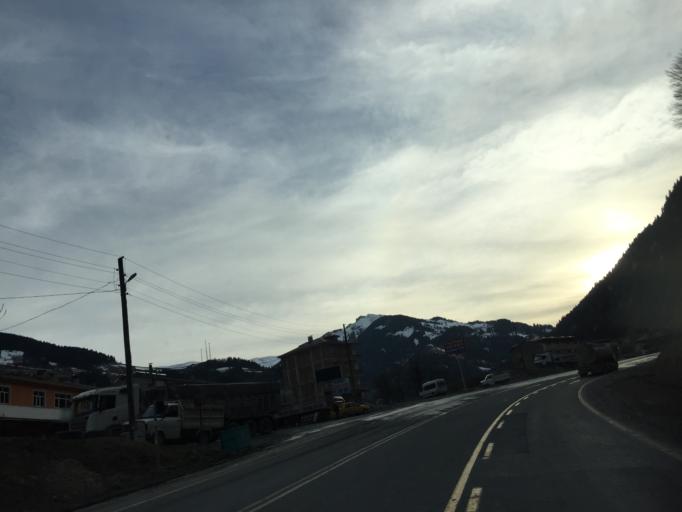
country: TR
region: Trabzon
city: Macka
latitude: 40.7099
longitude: 39.5006
